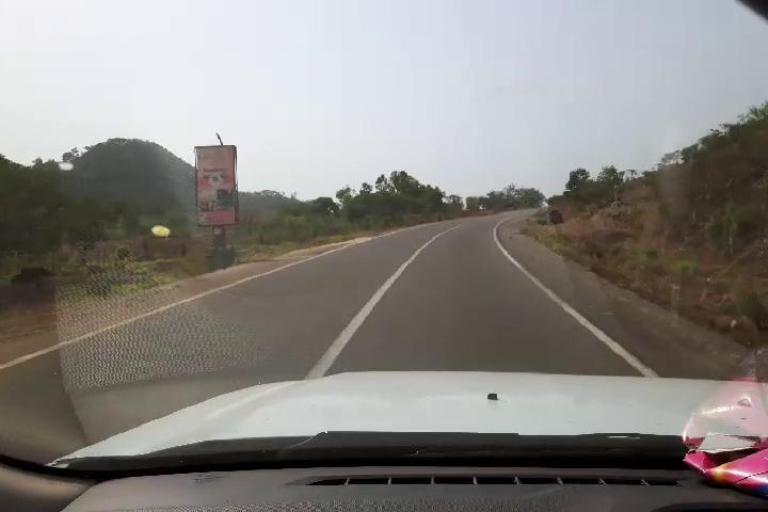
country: SL
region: Western Area
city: Waterloo
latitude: 8.2081
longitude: -13.1325
